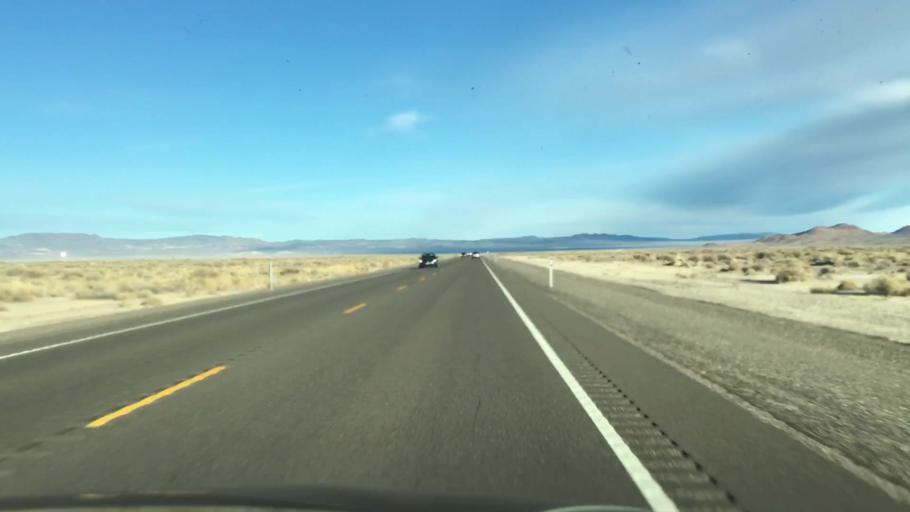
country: US
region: Nevada
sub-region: Nye County
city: Tonopah
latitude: 38.1297
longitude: -117.5635
